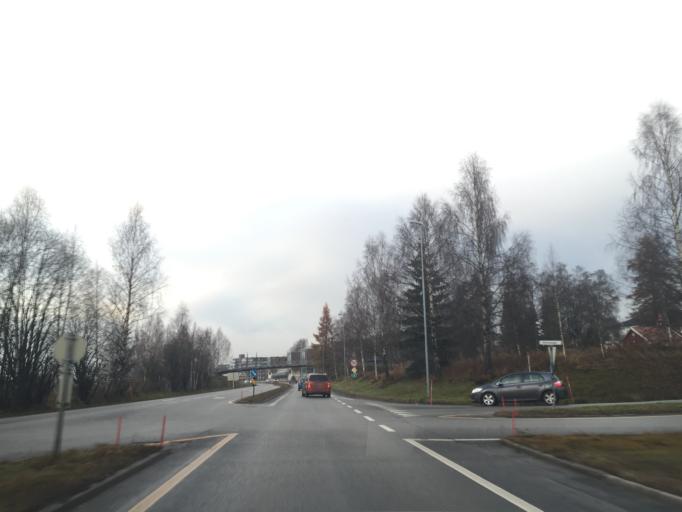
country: NO
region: Hedmark
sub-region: Elverum
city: Elverum
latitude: 60.8776
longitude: 11.5606
